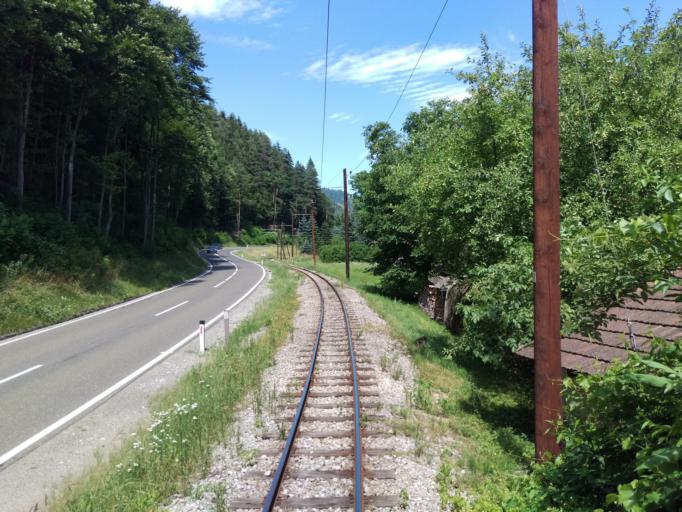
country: AT
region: Styria
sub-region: Politischer Bezirk Bruck-Muerzzuschlag
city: Pernegg an der Mur
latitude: 47.3492
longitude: 15.3647
